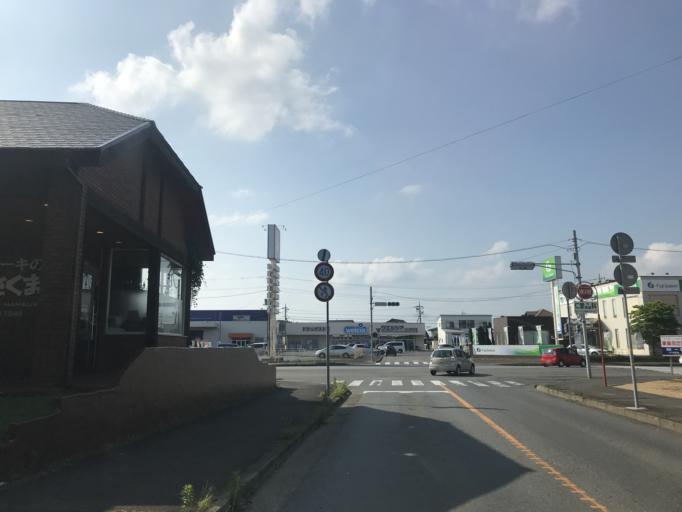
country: JP
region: Ibaraki
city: Naka
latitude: 36.0717
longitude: 140.0953
